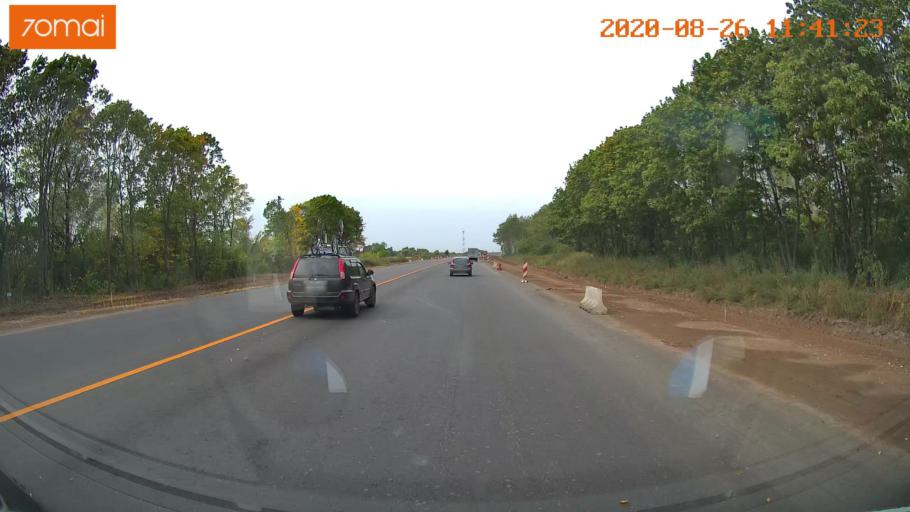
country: RU
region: Rjazan
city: Shilovo
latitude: 54.2952
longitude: 40.7126
